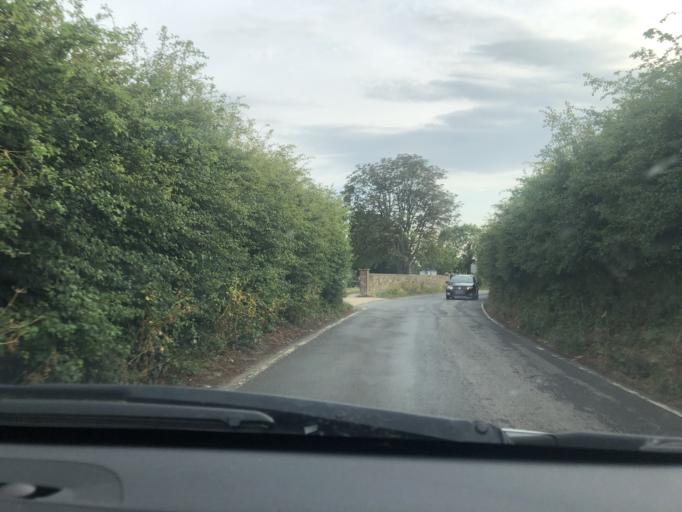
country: GB
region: England
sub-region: Kent
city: Herne Bay
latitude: 51.3689
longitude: 1.1774
